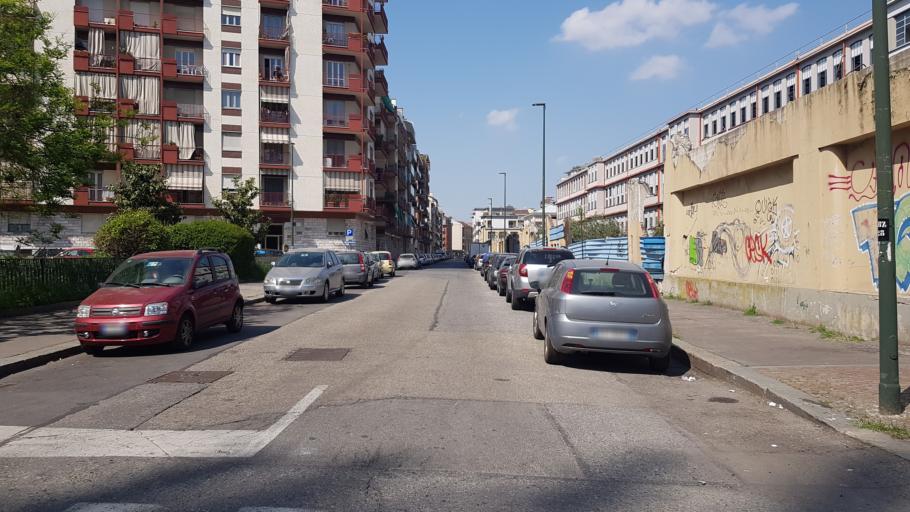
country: IT
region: Piedmont
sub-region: Provincia di Torino
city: Lesna
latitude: 45.0613
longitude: 7.6399
